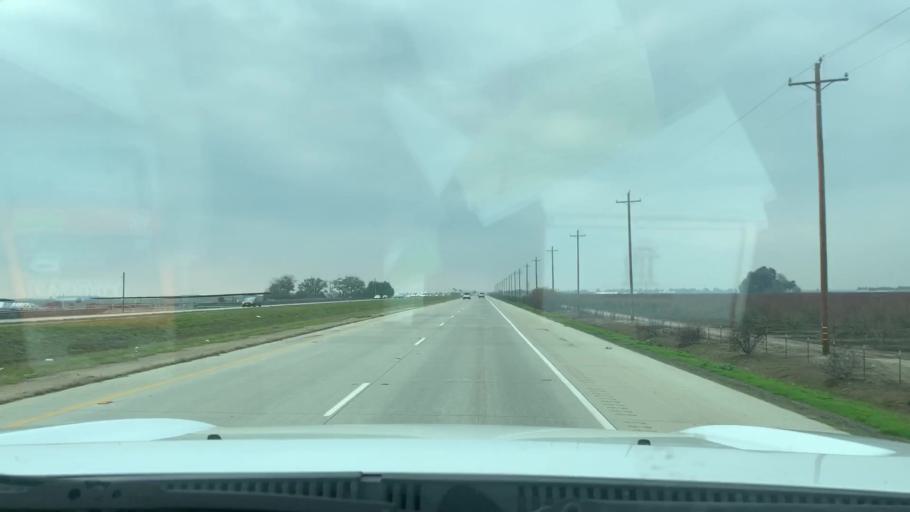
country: US
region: California
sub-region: Tulare County
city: Goshen
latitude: 36.3286
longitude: -119.4978
